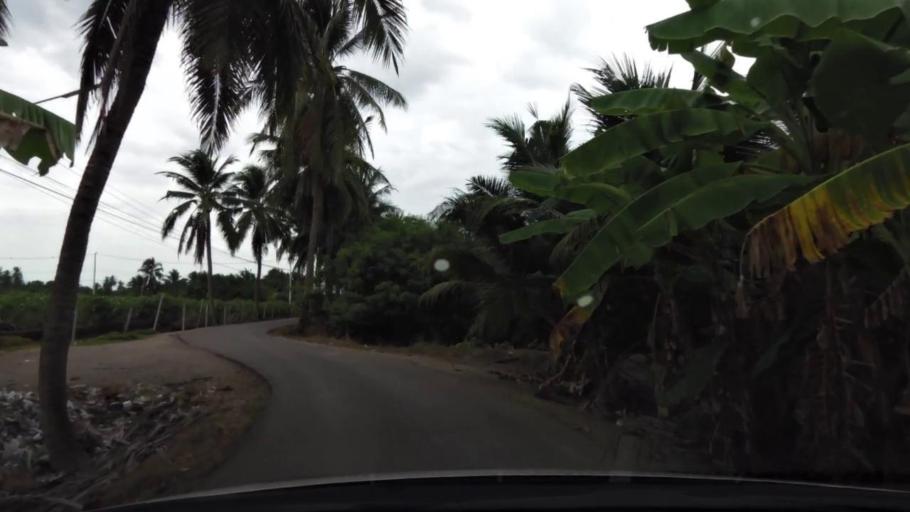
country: TH
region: Ratchaburi
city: Damnoen Saduak
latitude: 13.5725
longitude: 99.9797
